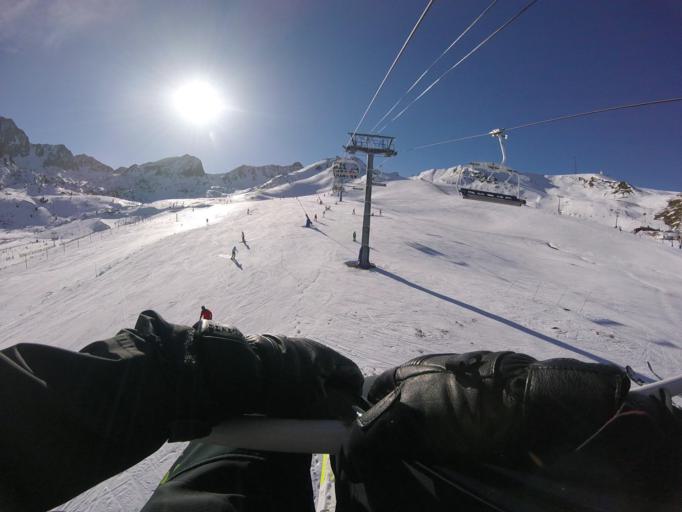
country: AD
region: Encamp
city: Pas de la Casa
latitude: 42.5375
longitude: 1.7317
